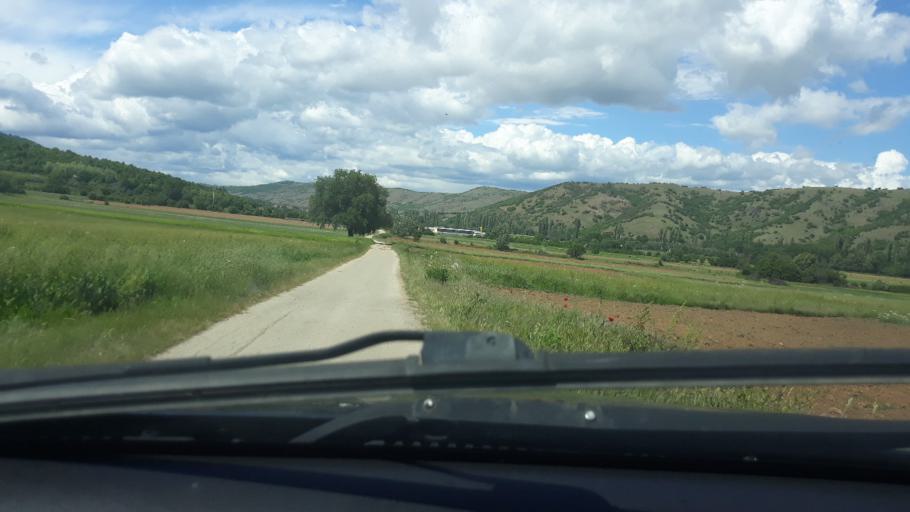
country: MK
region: Krivogastani
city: Krivogashtani
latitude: 41.3423
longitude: 21.2993
